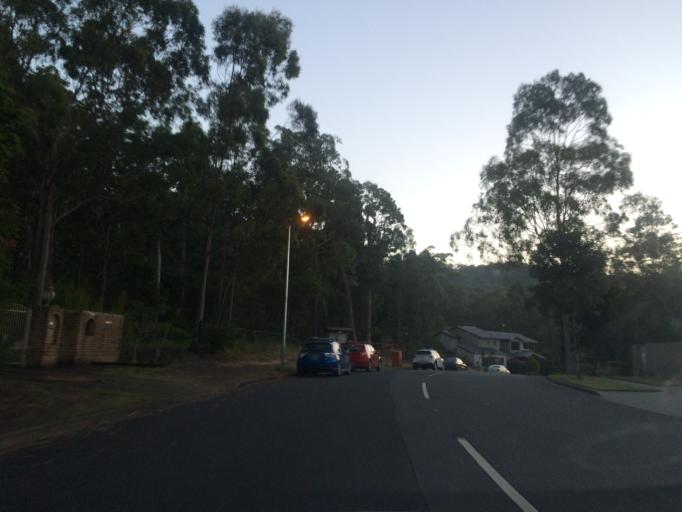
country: AU
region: Queensland
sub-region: Brisbane
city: Kenmore Hills
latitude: -27.4828
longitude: 152.9370
